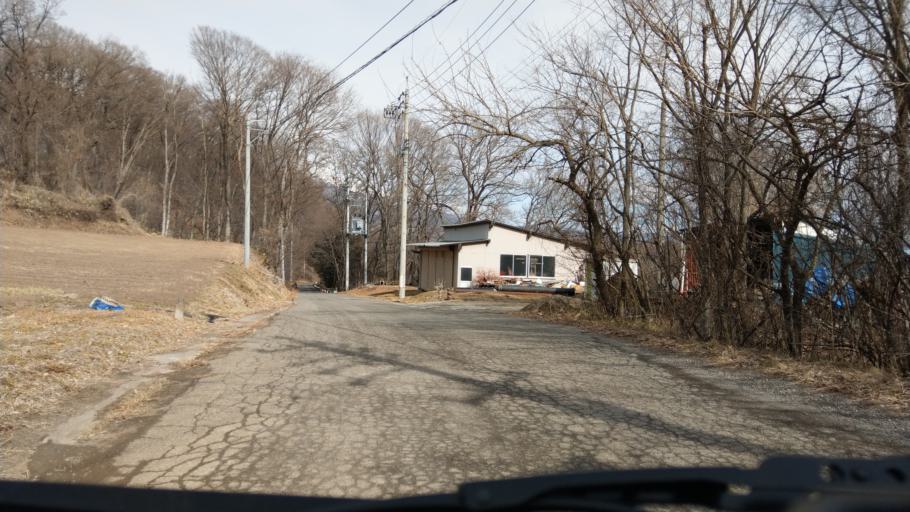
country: JP
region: Nagano
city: Komoro
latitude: 36.2854
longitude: 138.4127
